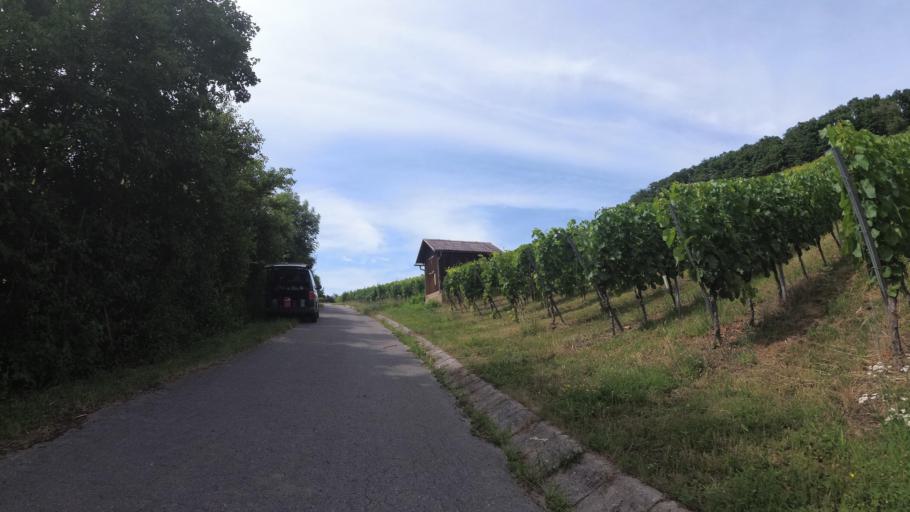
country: DE
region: Baden-Wuerttemberg
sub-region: Regierungsbezirk Stuttgart
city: Eberstadt
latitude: 49.1890
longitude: 9.3157
